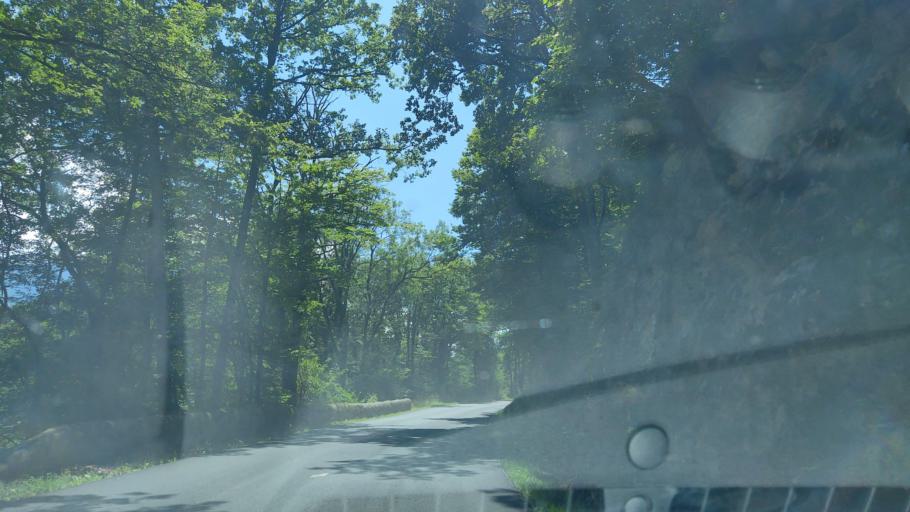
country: FR
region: Rhone-Alpes
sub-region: Departement de la Savoie
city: Aiton
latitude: 45.5217
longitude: 6.3052
